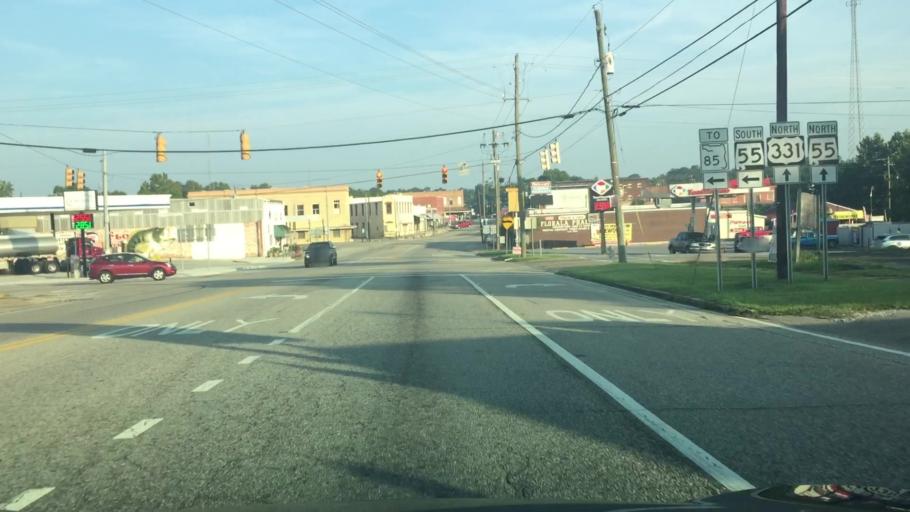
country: US
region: Alabama
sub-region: Covington County
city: Florala
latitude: 31.0044
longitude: -86.3262
